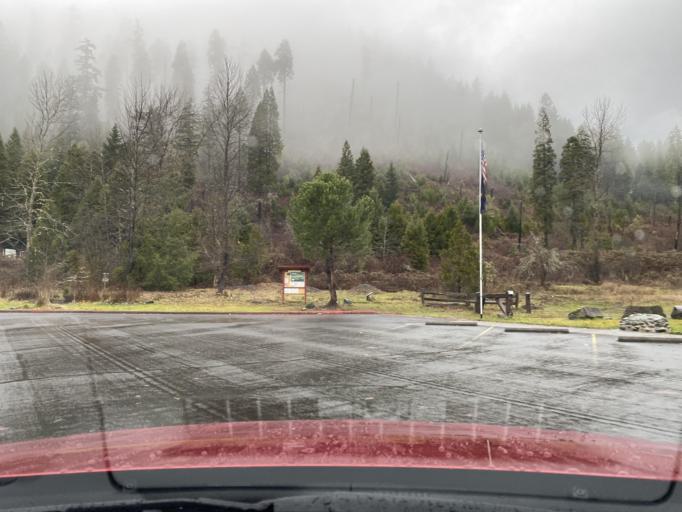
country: US
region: Oregon
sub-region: Lane County
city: Oakridge
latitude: 43.7591
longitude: -122.4959
